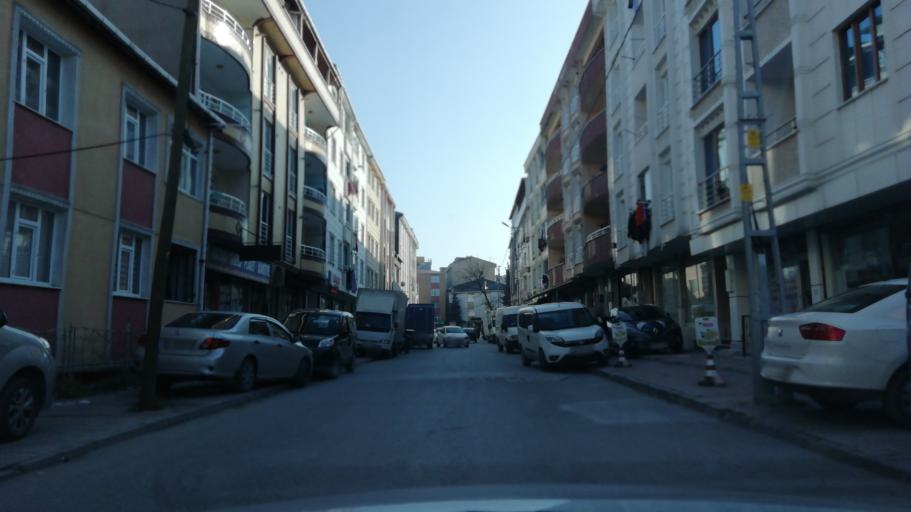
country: TR
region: Istanbul
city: Esenyurt
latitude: 41.0336
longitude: 28.6893
